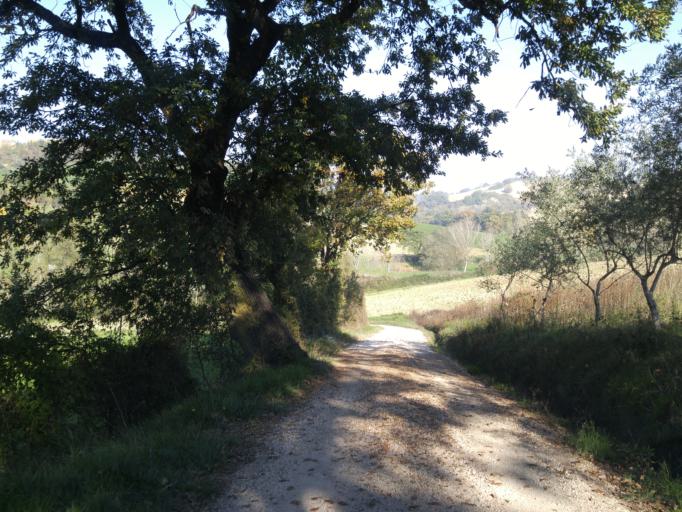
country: IT
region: The Marches
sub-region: Provincia di Pesaro e Urbino
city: Montemaggiore al Metauro
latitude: 43.7346
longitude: 12.9533
